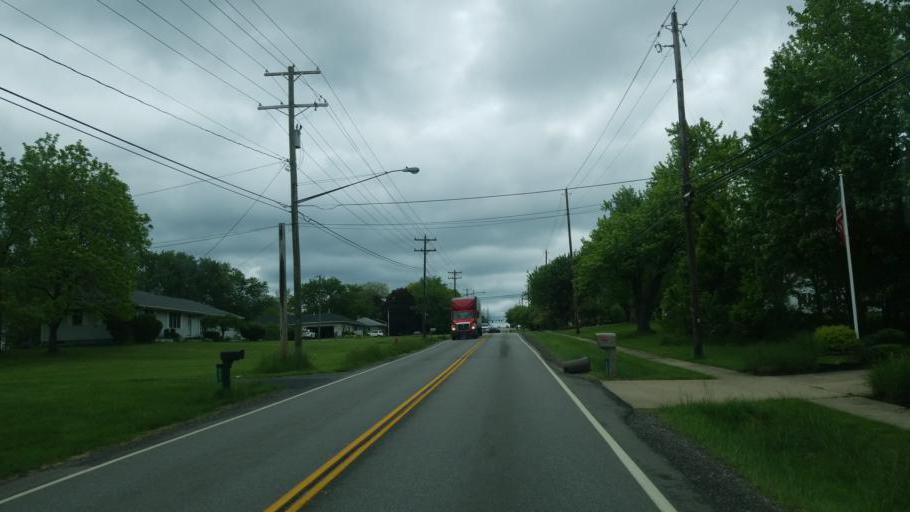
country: US
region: Ohio
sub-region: Medina County
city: Brunswick
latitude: 41.2382
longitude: -81.8489
